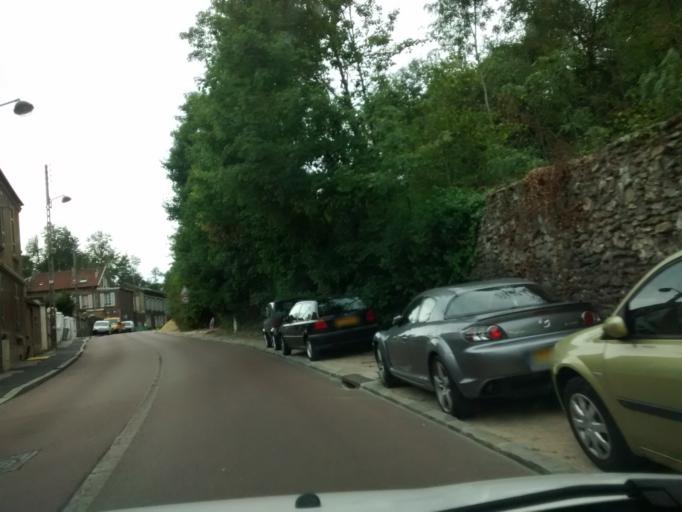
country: FR
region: Ile-de-France
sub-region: Departement des Yvelines
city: Versailles
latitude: 48.7910
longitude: 2.1356
